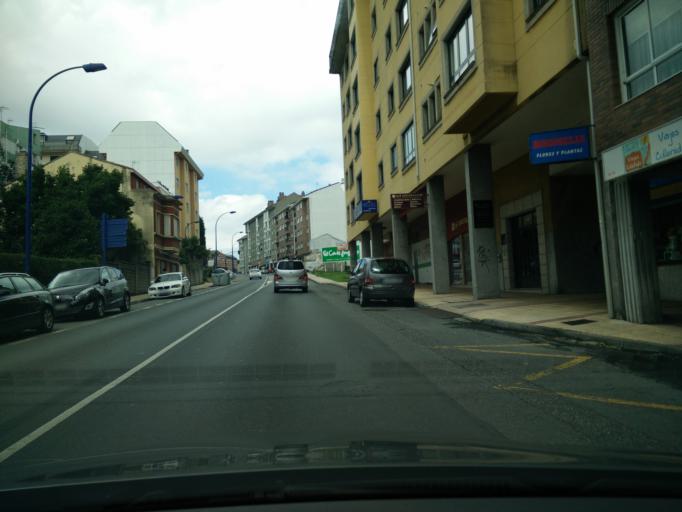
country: ES
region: Galicia
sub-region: Provincia da Coruna
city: Culleredo
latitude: 43.3161
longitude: -8.3835
